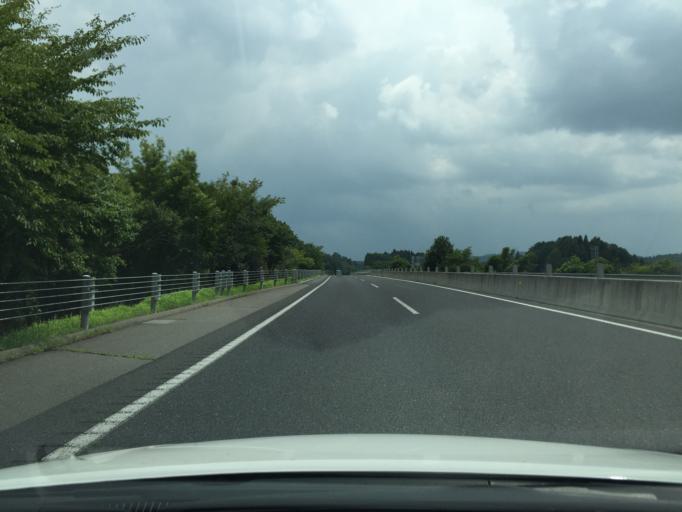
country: JP
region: Fukushima
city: Funehikimachi-funehiki
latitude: 37.3073
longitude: 140.6112
